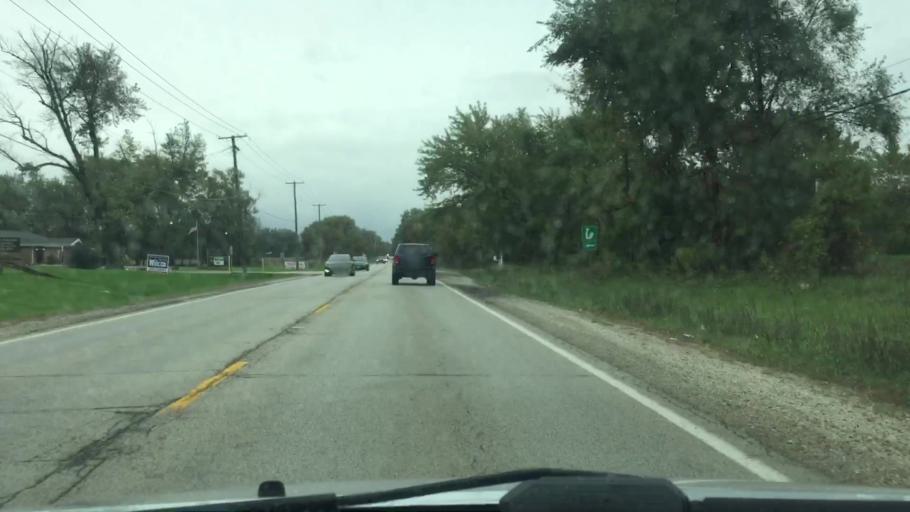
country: US
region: Illinois
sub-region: McHenry County
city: Richmond
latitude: 42.4657
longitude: -88.3068
